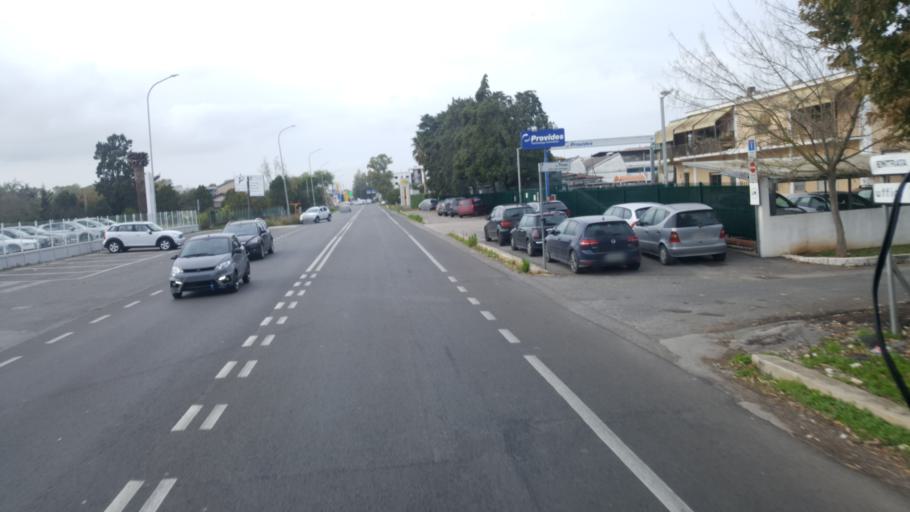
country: IT
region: Latium
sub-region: Provincia di Latina
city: Latina
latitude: 41.4796
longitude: 12.8699
